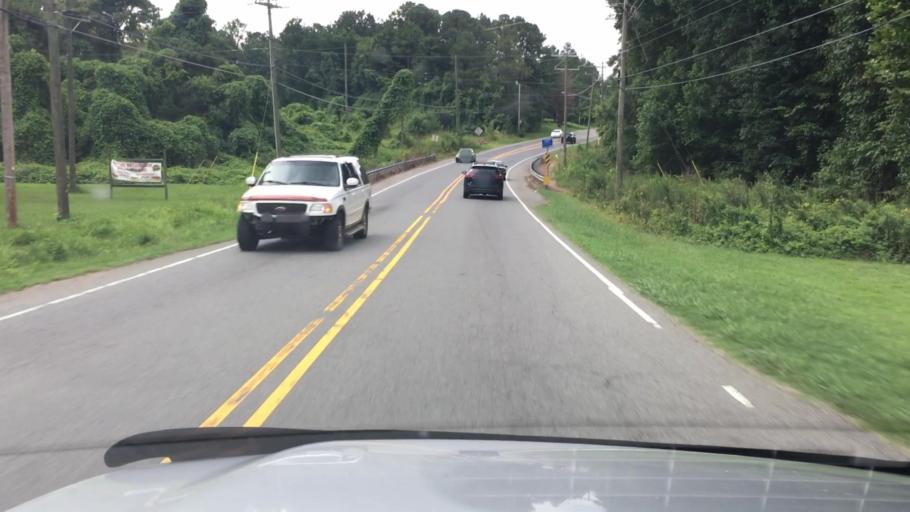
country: US
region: North Carolina
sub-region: Mecklenburg County
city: Huntersville
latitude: 35.3198
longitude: -80.8650
